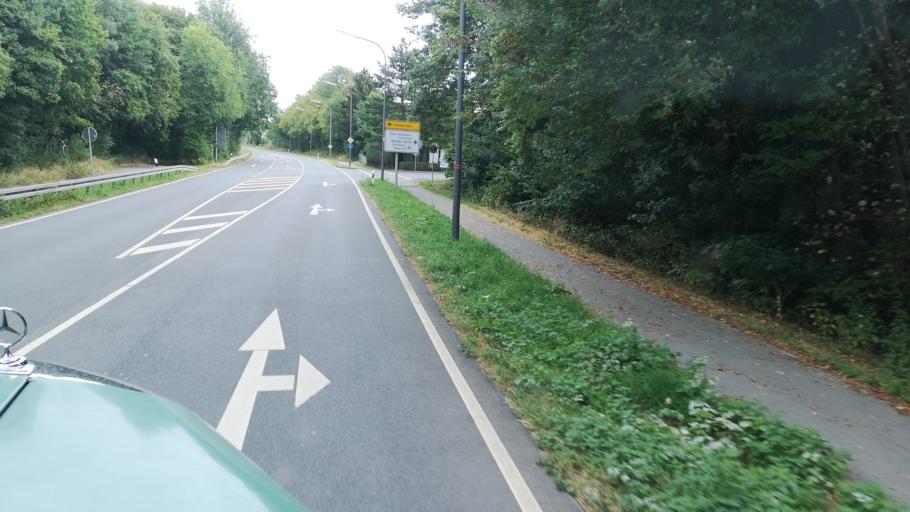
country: DE
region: North Rhine-Westphalia
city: Wermelskirchen
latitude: 51.0960
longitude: 7.1975
